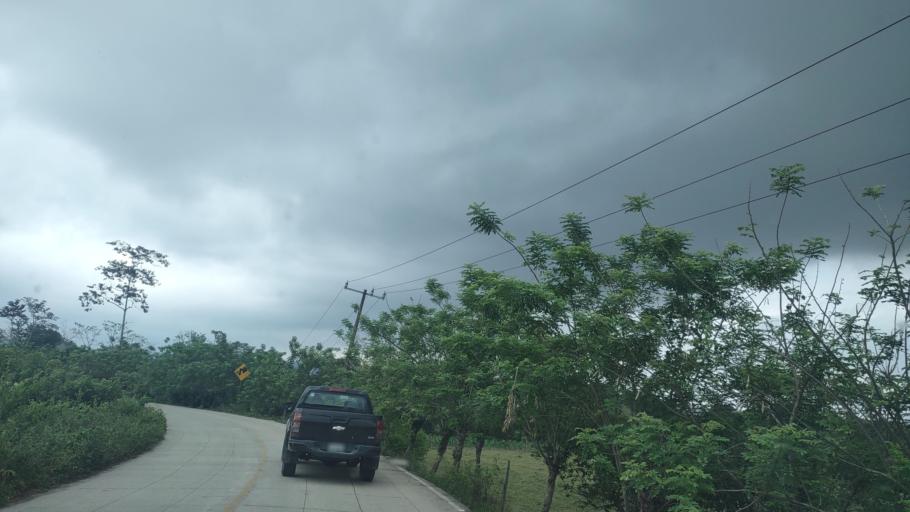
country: MX
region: Veracruz
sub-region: Uxpanapa
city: Poblado 10
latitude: 17.4945
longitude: -94.1738
